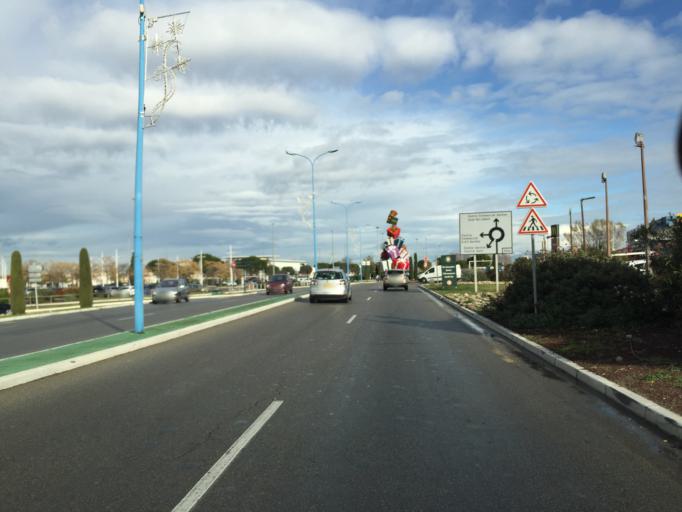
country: FR
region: Provence-Alpes-Cote d'Azur
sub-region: Departement du Vaucluse
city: Le Pontet
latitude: 43.9787
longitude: 4.8778
